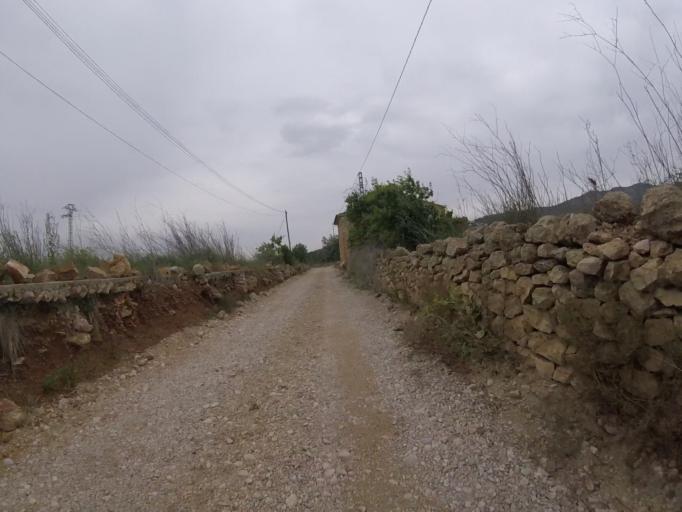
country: ES
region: Valencia
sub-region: Provincia de Castello
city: Alcoceber
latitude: 40.2413
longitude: 0.2687
